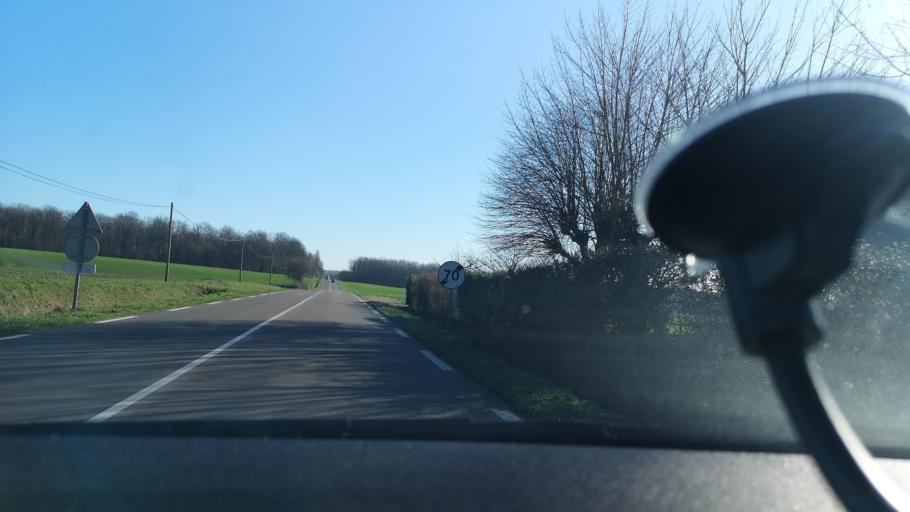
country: FR
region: Bourgogne
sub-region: Departement de Saone-et-Loire
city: Ouroux-sur-Saone
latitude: 46.7689
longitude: 4.9795
